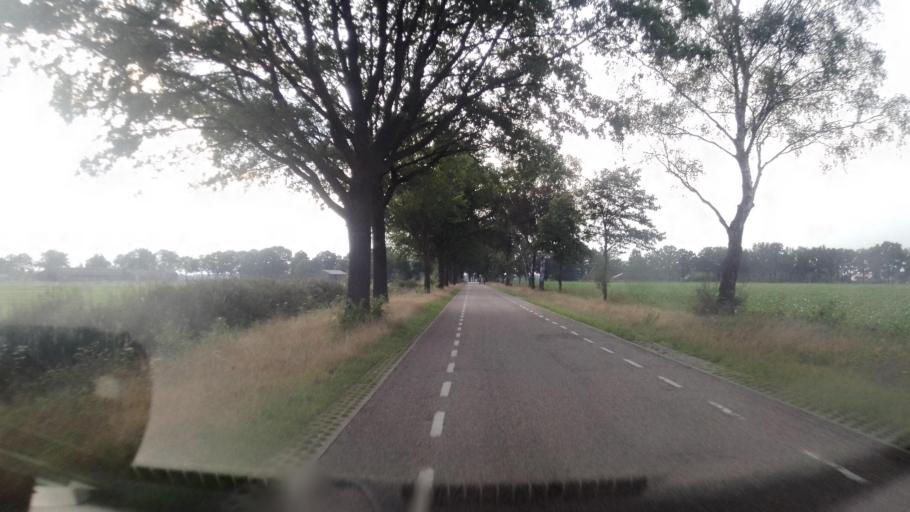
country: NL
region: Limburg
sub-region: Gemeente Peel en Maas
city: Maasbree
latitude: 51.3949
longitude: 5.9595
